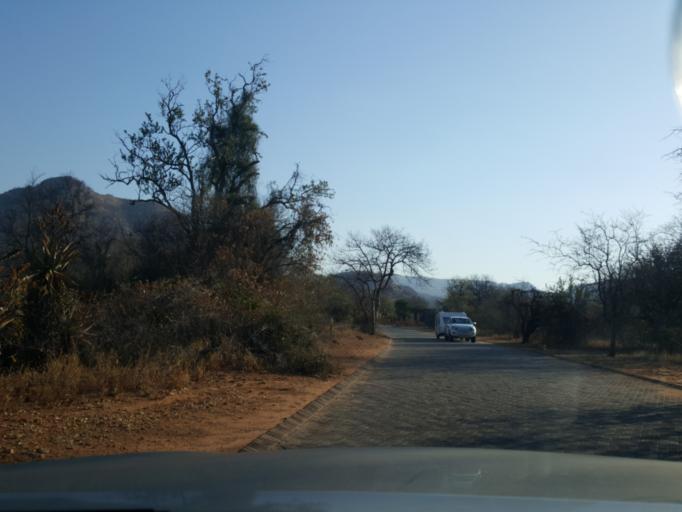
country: SZ
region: Hhohho
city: Ntfonjeni
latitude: -25.4276
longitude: 31.4460
